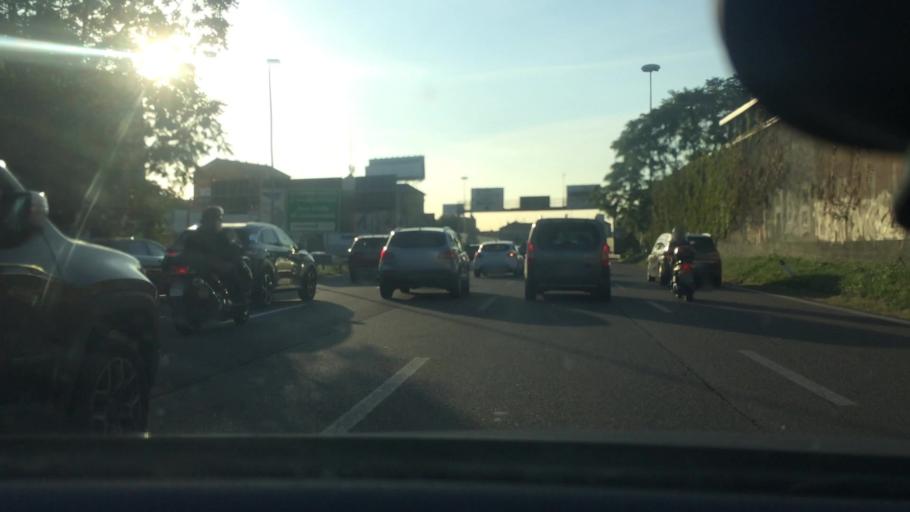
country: IT
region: Lombardy
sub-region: Citta metropolitana di Milano
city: Baranzate
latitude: 45.5130
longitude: 9.1246
